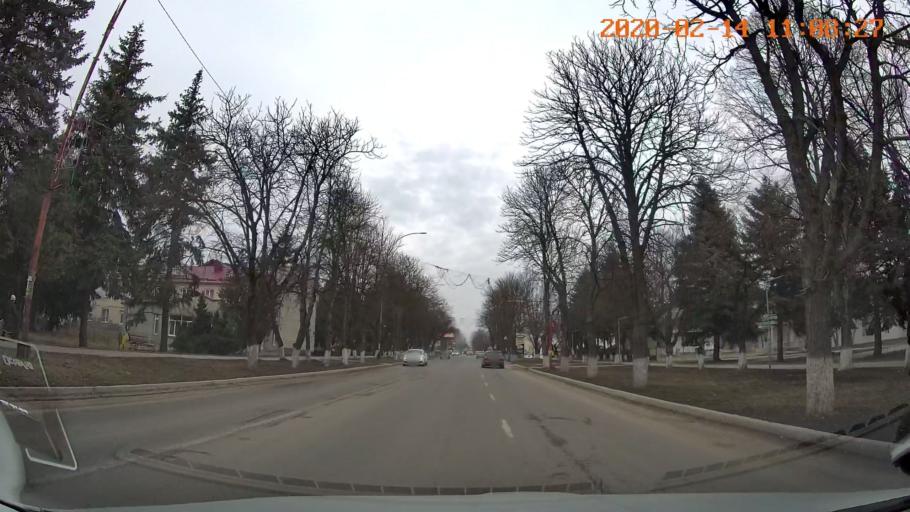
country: MD
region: Raionul Edinet
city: Edinet
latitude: 48.1721
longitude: 27.3020
